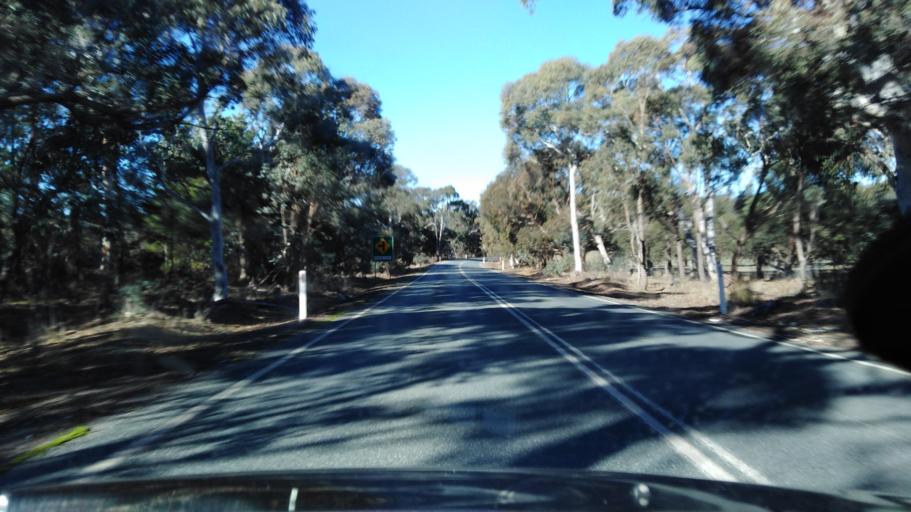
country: AU
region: New South Wales
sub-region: Palerang
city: Bungendore
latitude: -35.1884
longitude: 149.3279
